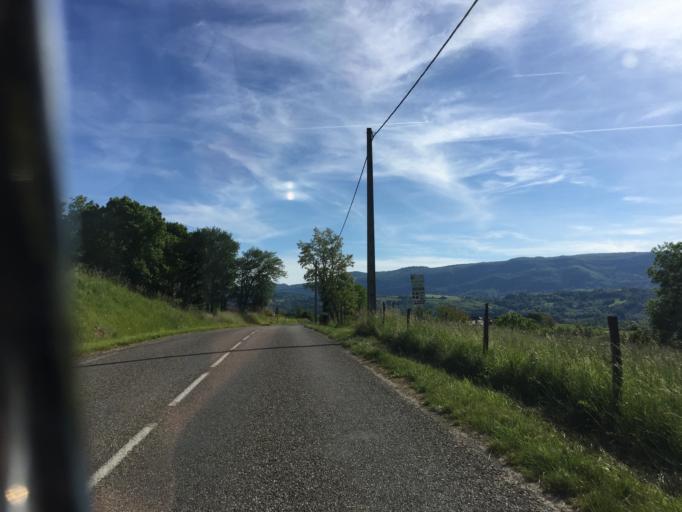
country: FR
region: Rhone-Alpes
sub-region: Departement de la Haute-Savoie
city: Sales
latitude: 45.8933
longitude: 5.9613
